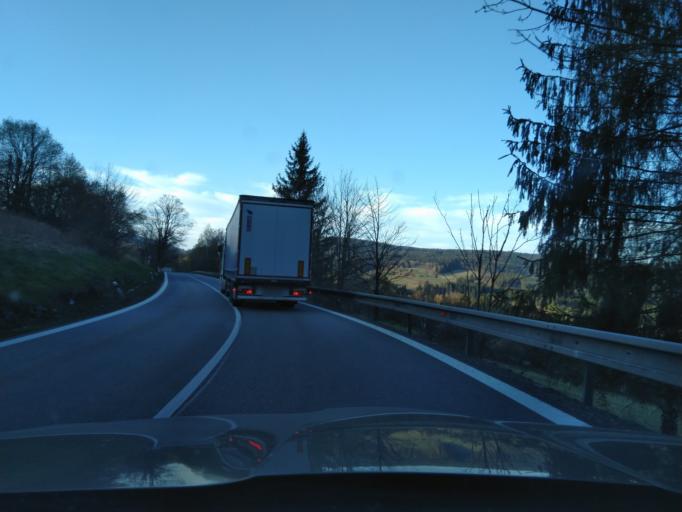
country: CZ
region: Jihocesky
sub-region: Okres Prachatice
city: Vimperk
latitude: 49.0359
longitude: 13.7618
